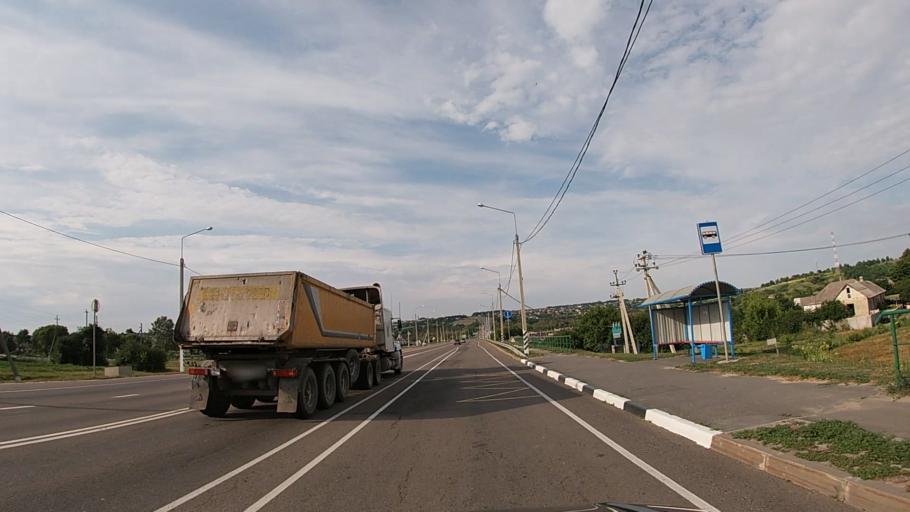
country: RU
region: Belgorod
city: Severnyy
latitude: 50.6393
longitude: 36.4681
